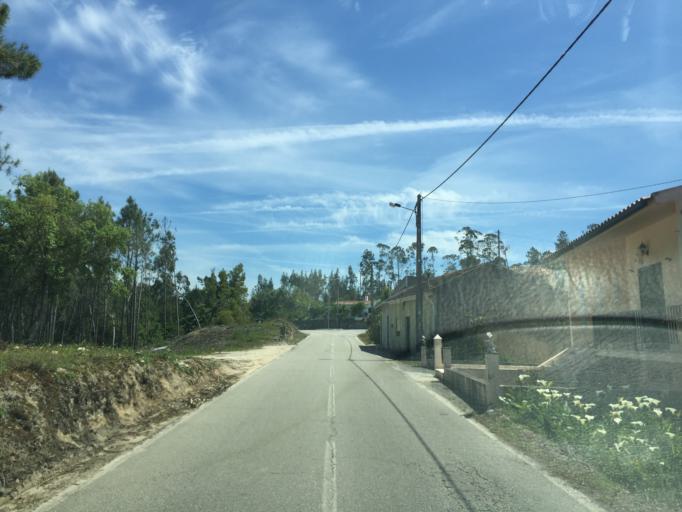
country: PT
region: Leiria
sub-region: Pombal
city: Lourical
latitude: 40.0645
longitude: -8.7148
